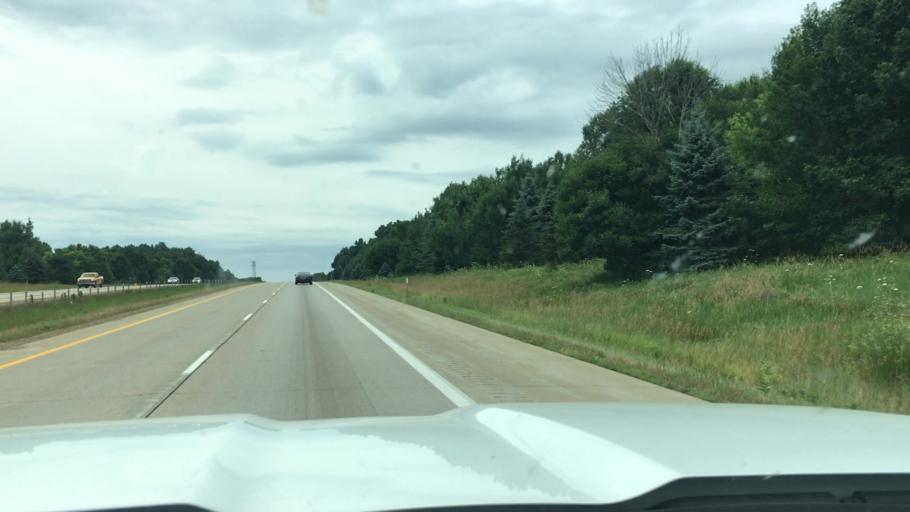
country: US
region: Michigan
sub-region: Allegan County
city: Otsego
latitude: 42.5074
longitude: -85.6544
